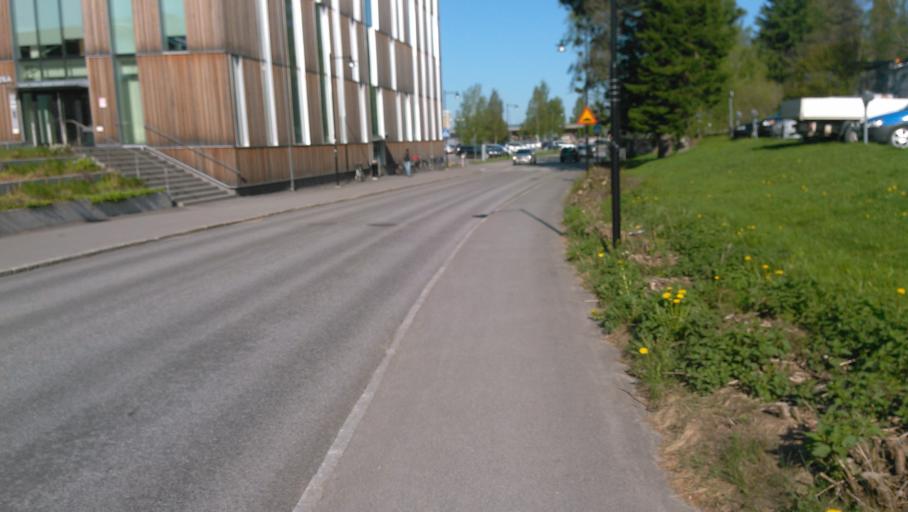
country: SE
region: Vaesterbotten
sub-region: Umea Kommun
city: Umea
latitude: 63.8214
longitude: 20.2743
